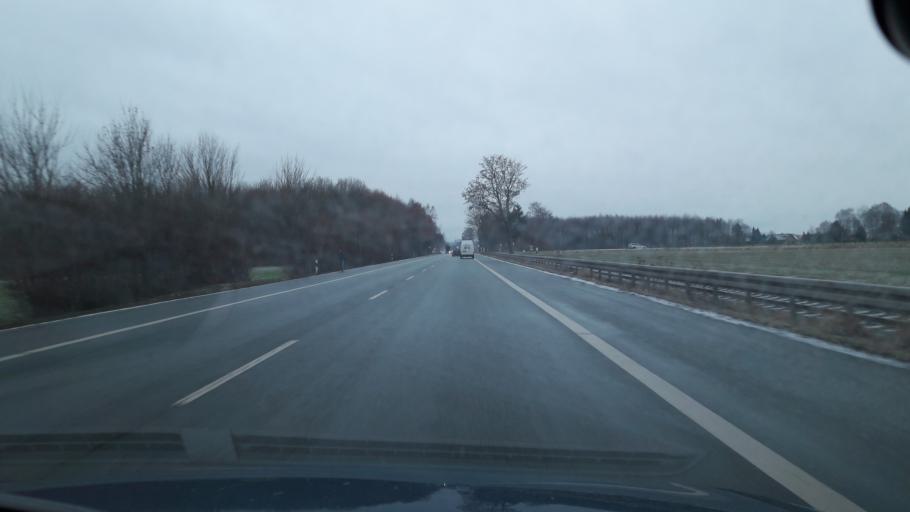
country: DE
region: North Rhine-Westphalia
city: Erwitte
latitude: 51.6230
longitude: 8.3379
